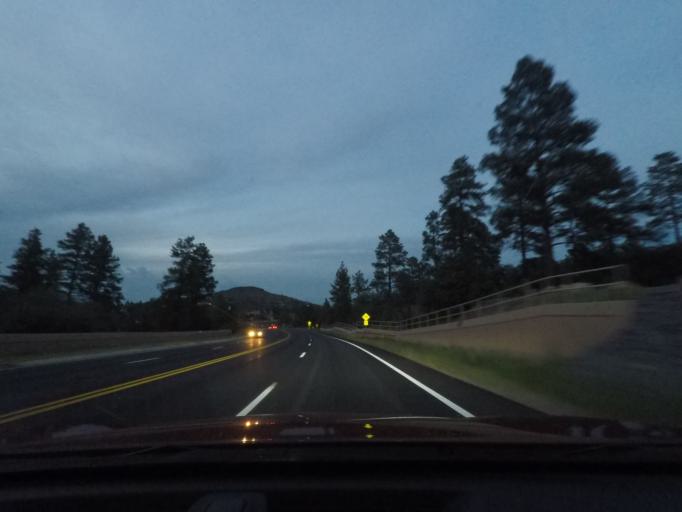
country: US
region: Arizona
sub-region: Yavapai County
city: Prescott
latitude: 34.5859
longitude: -112.4990
